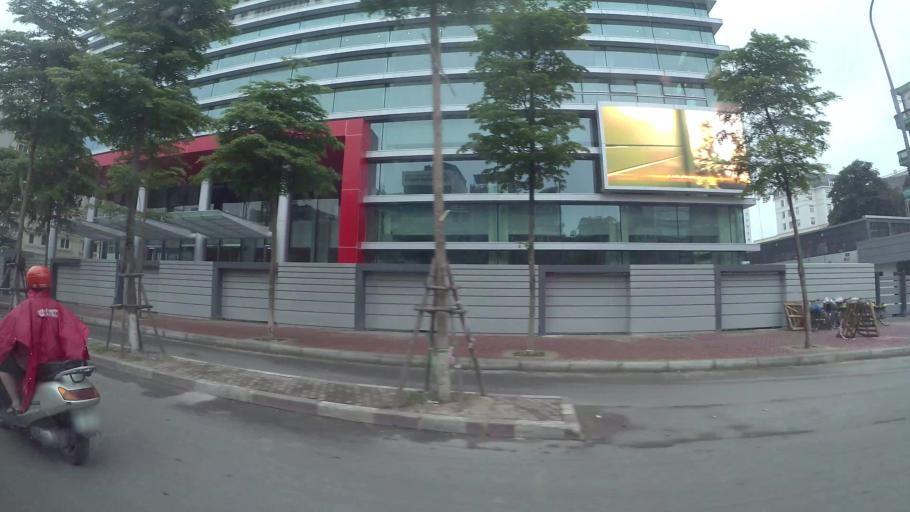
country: VN
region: Ha Noi
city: Dong Da
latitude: 21.0147
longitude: 105.8334
